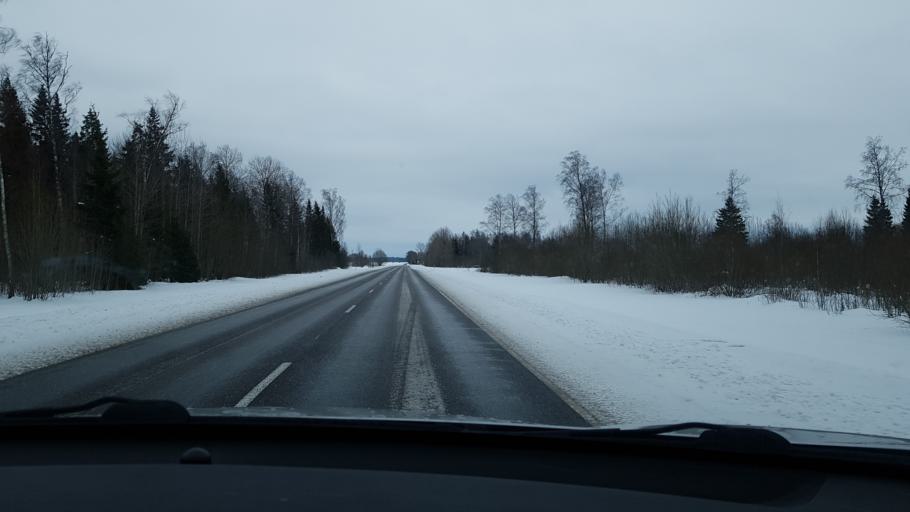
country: EE
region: Jaervamaa
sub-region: Jaerva-Jaani vald
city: Jarva-Jaani
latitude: 59.1293
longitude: 25.7804
